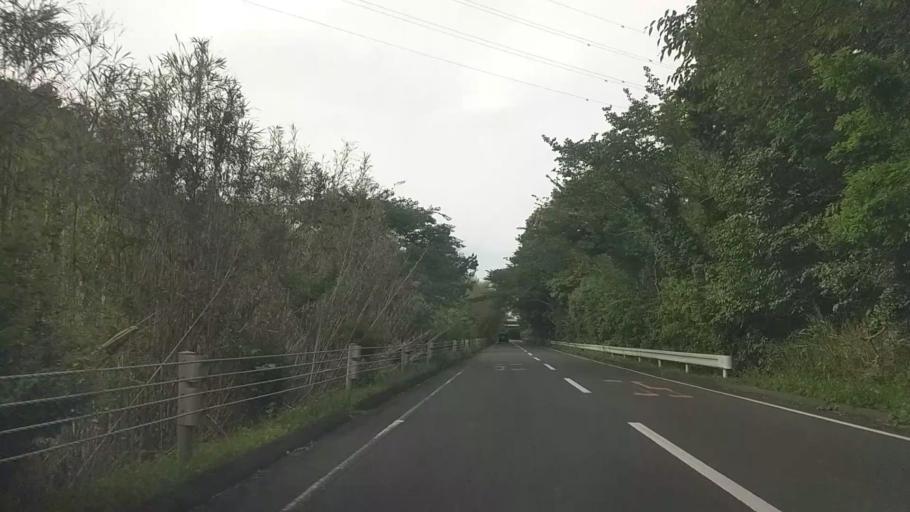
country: JP
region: Shizuoka
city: Kosai-shi
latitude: 34.7524
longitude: 137.6115
